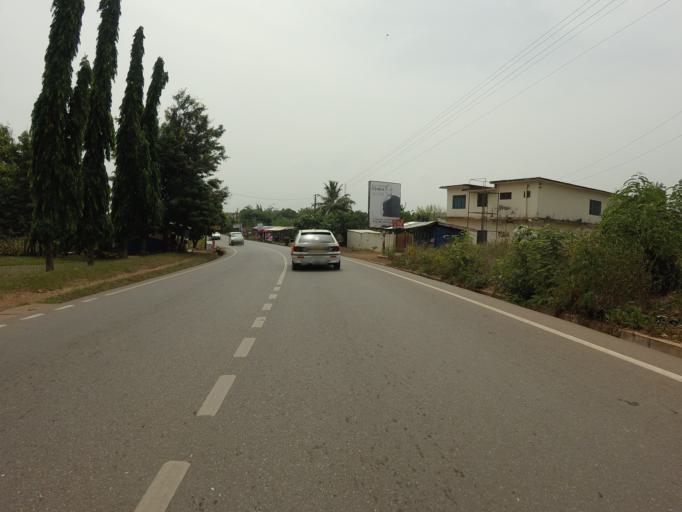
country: GH
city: Akropong
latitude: 6.0928
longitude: -0.0213
